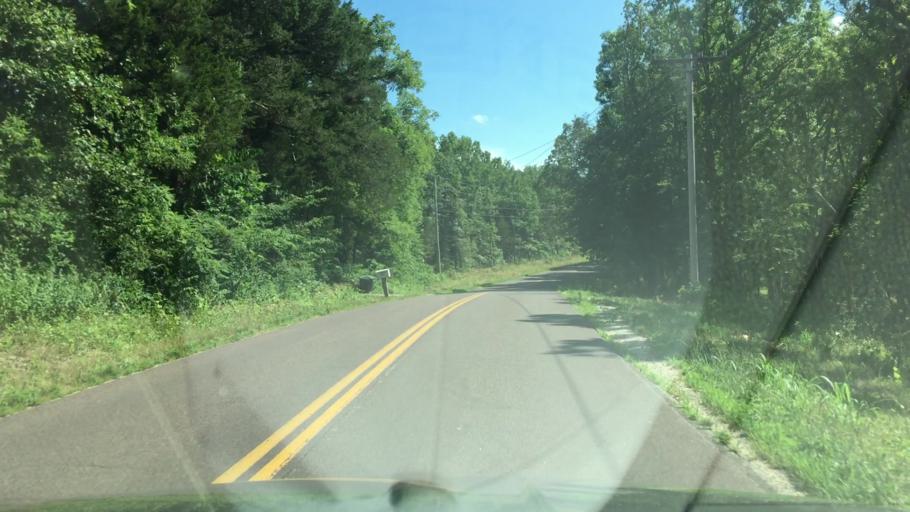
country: US
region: Missouri
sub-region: Miller County
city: Tuscumbia
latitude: 38.0932
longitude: -92.4803
